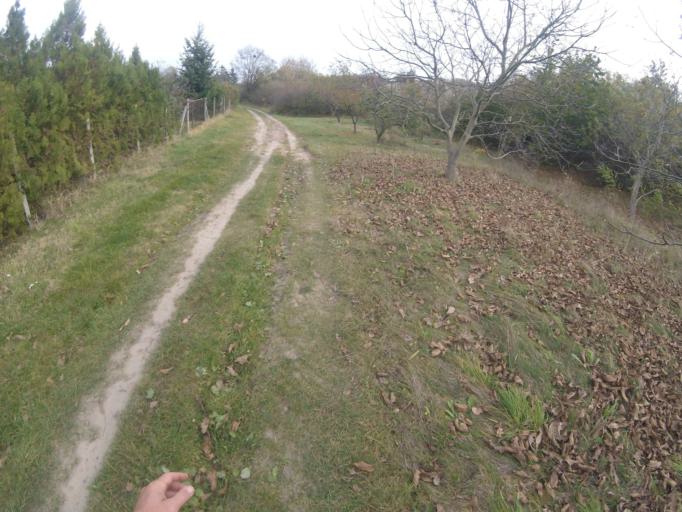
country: HU
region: Fejer
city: Bodajk
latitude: 47.3200
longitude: 18.2208
